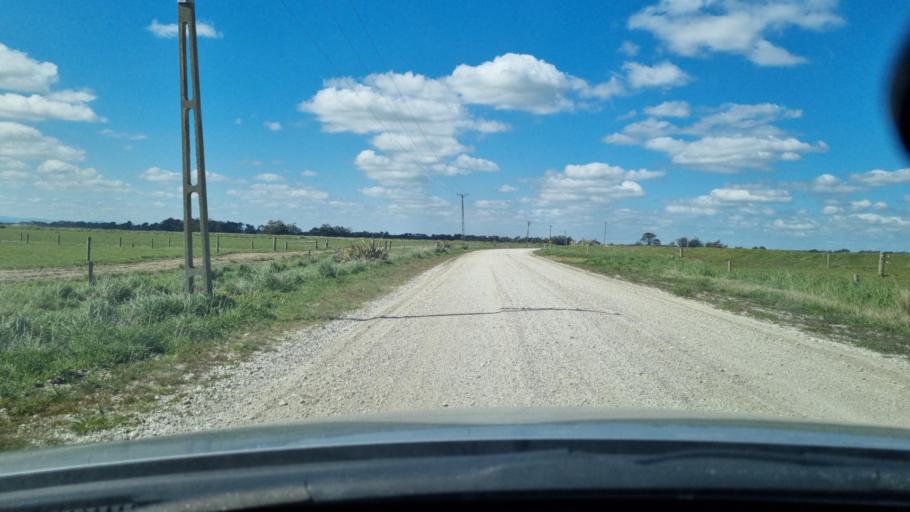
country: NZ
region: Southland
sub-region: Invercargill City
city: Invercargill
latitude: -46.3912
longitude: 168.2553
